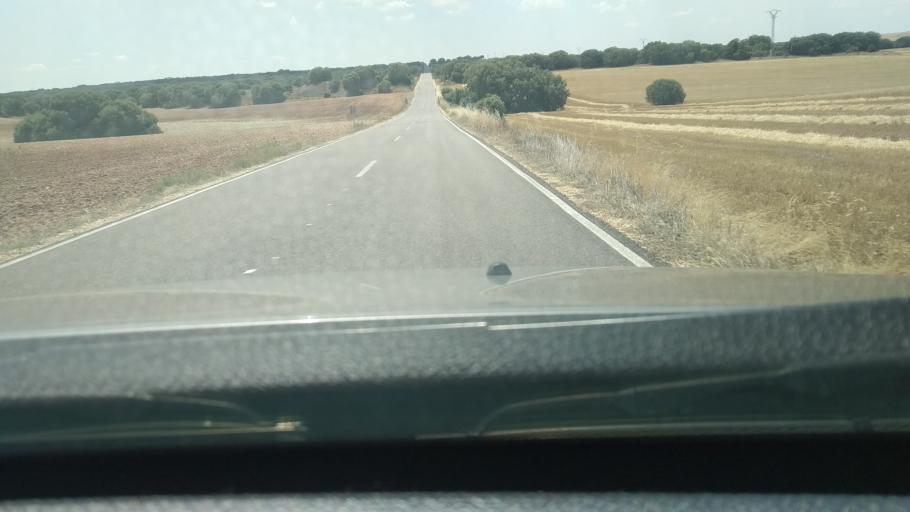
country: ES
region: Castille and Leon
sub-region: Provincia de Burgos
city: Avellanosa de Muno
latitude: 41.9719
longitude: -3.8104
